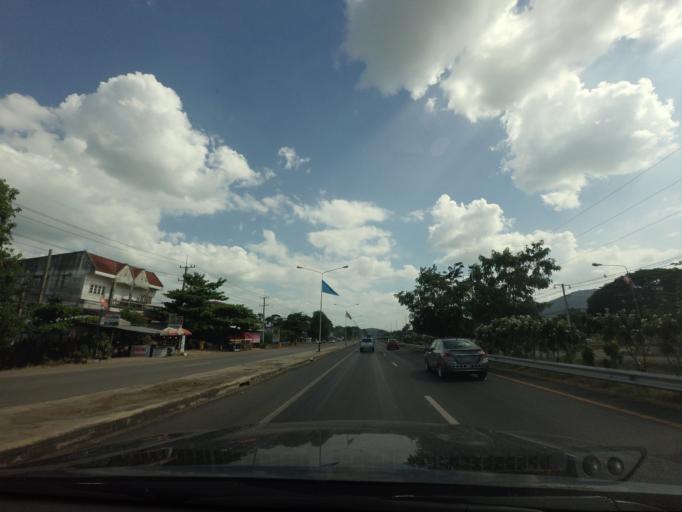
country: TH
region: Phetchabun
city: Wichian Buri
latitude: 15.6496
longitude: 101.0414
